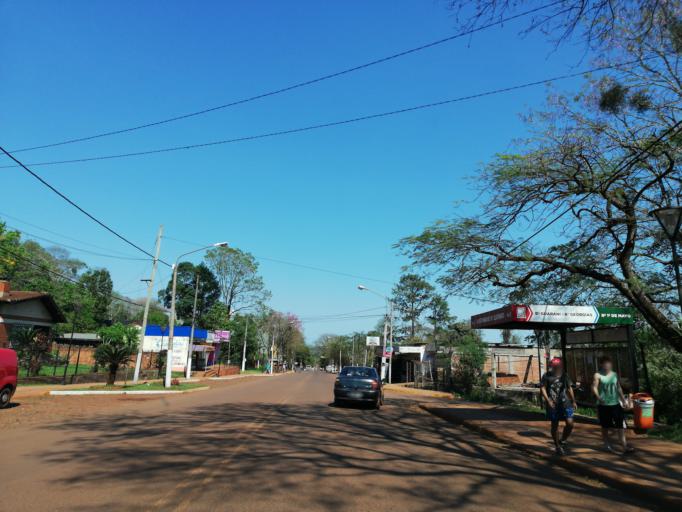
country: AR
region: Misiones
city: Puerto Eldorado
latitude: -26.4073
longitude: -54.6684
